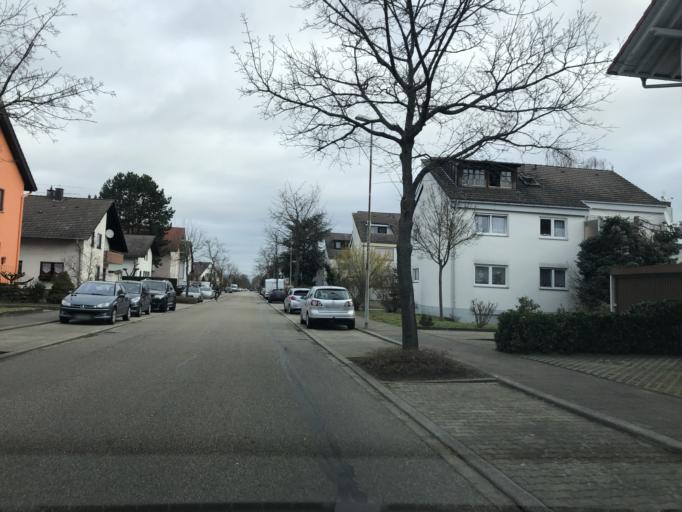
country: DE
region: Baden-Wuerttemberg
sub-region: Karlsruhe Region
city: Forst
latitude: 49.1572
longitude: 8.5819
